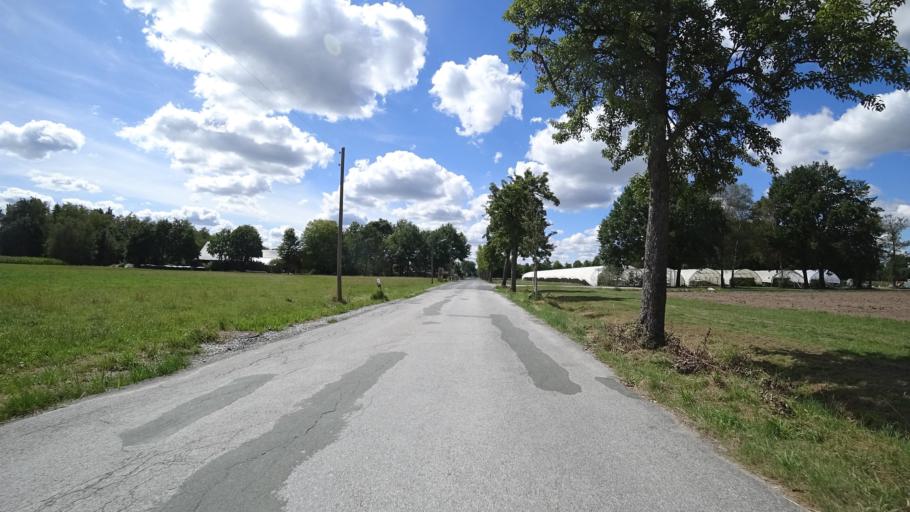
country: DE
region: North Rhine-Westphalia
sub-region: Regierungsbezirk Detmold
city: Steinhagen
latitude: 51.9618
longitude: 8.4317
